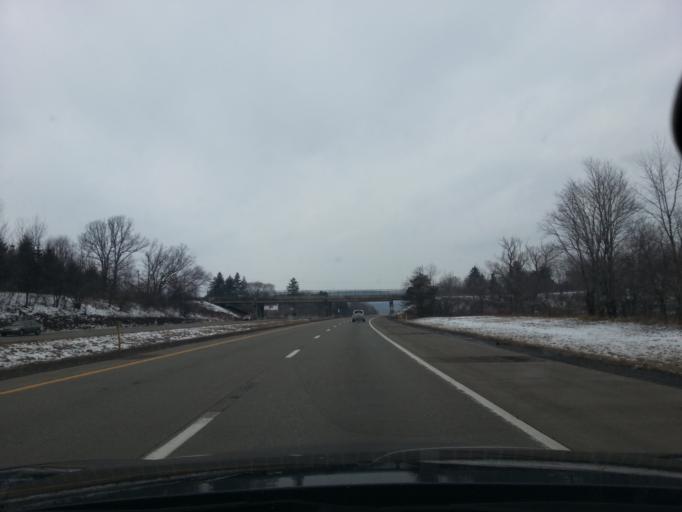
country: US
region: Pennsylvania
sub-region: Luzerne County
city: Harleigh
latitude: 41.0100
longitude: -76.0091
